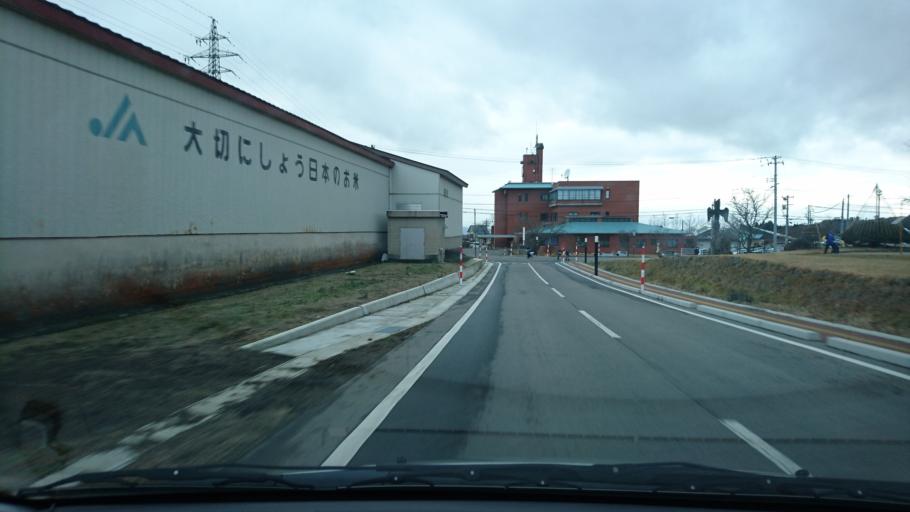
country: JP
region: Fukushima
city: Inawashiro
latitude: 37.5621
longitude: 139.9901
